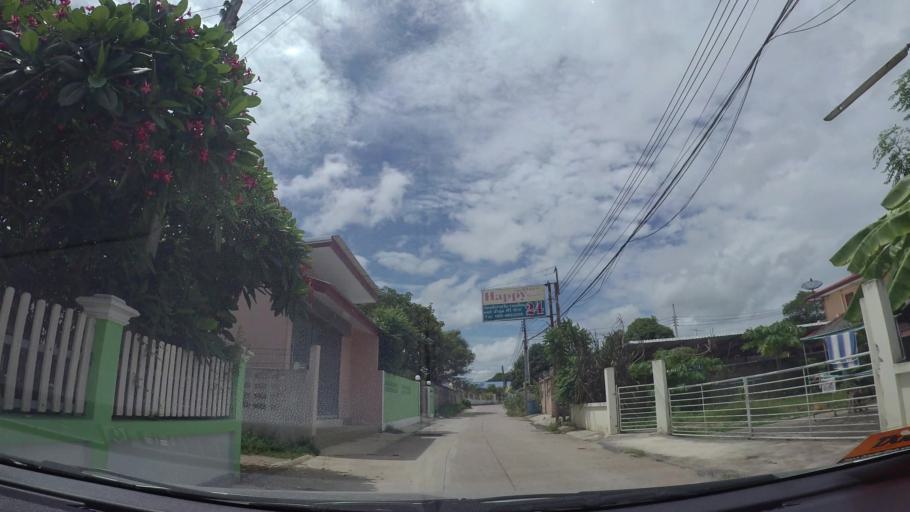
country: TH
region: Chon Buri
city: Sattahip
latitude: 12.6807
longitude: 100.8996
